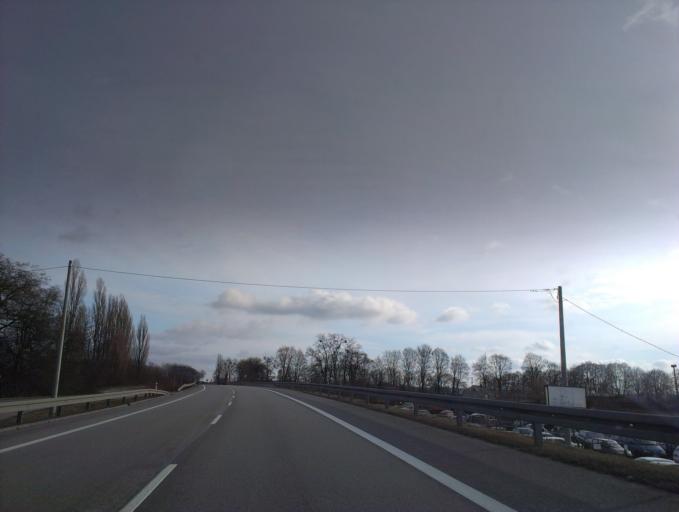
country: PL
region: Kujawsko-Pomorskie
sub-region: Powiat lipnowski
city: Lipno
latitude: 52.8555
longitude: 19.1619
